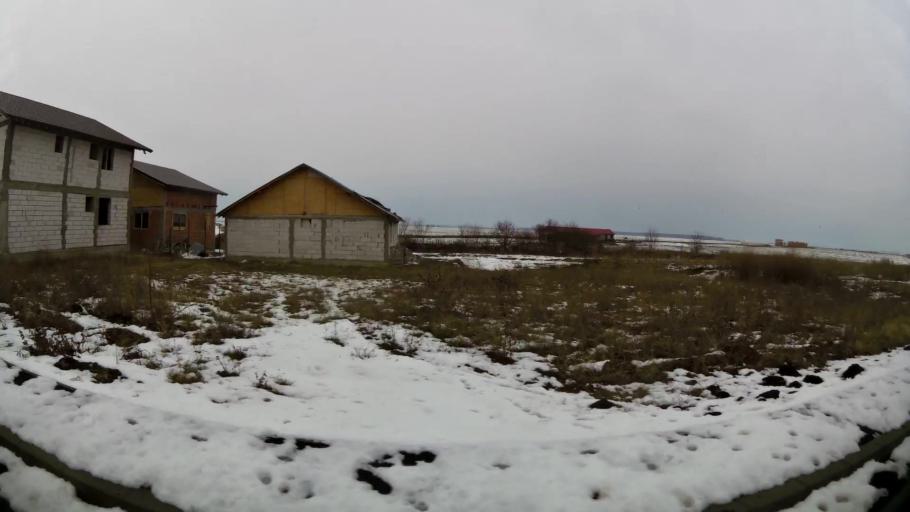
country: RO
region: Ilfov
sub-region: Comuna Tunari
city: Tunari
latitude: 44.5521
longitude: 26.1585
